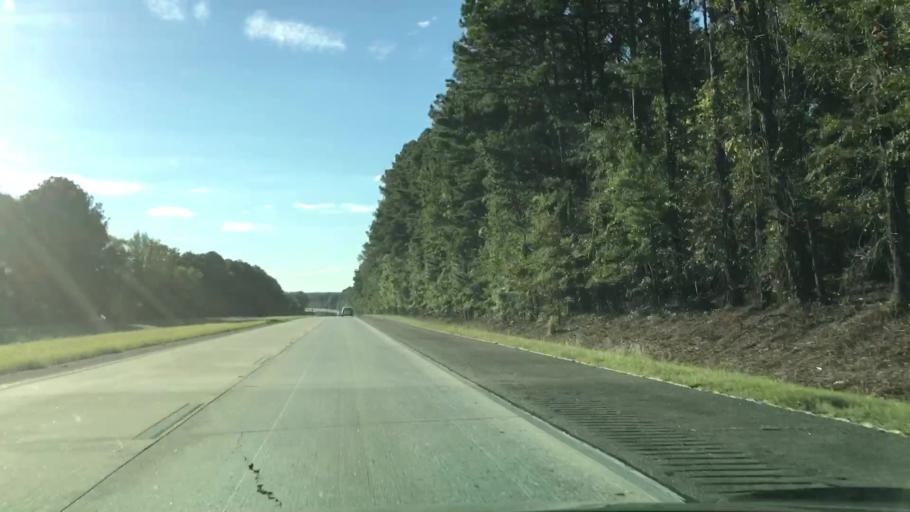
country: US
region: Georgia
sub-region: Greene County
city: Greensboro
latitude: 33.5483
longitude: -83.1189
